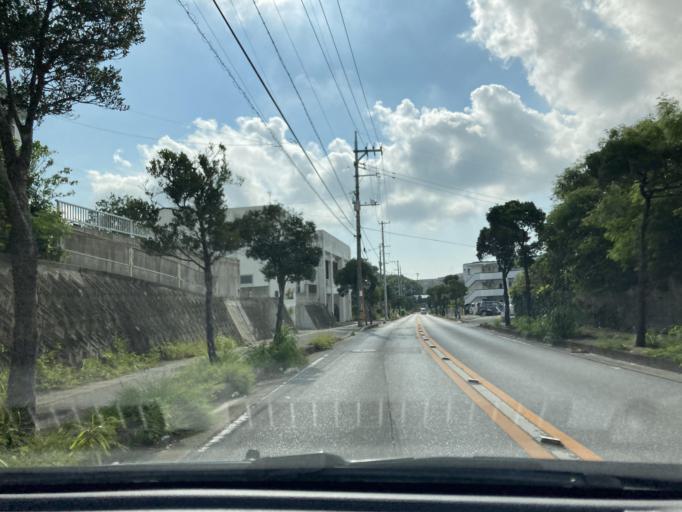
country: JP
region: Okinawa
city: Tomigusuku
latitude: 26.1478
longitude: 127.7615
